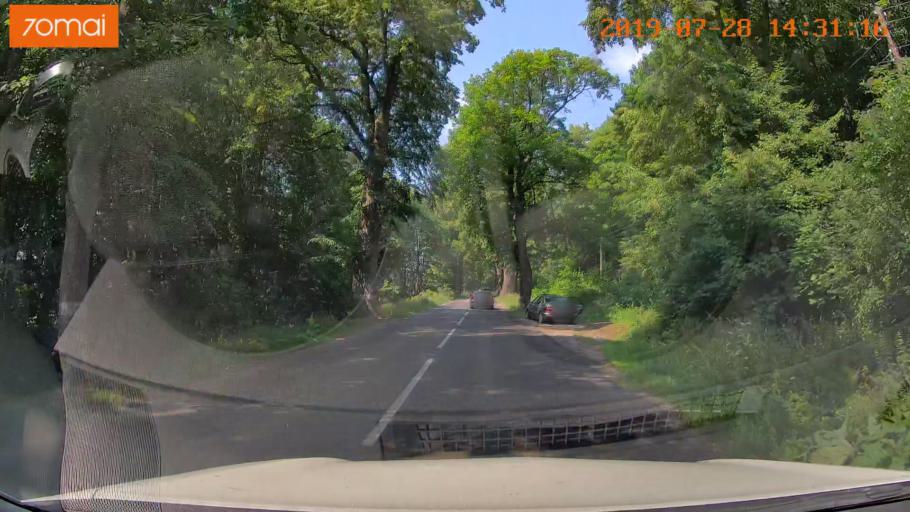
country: RU
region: Kaliningrad
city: Primorsk
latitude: 54.8052
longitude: 20.0529
